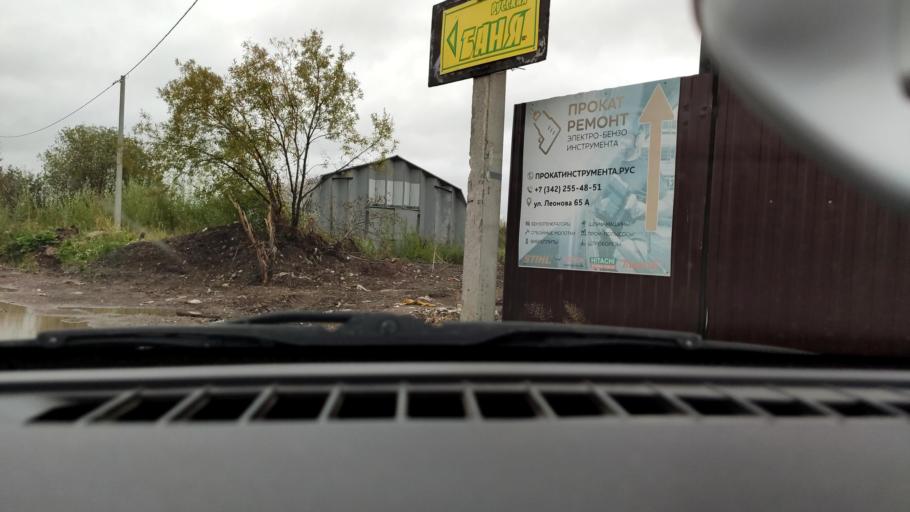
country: RU
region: Perm
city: Perm
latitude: 57.9546
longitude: 56.1882
